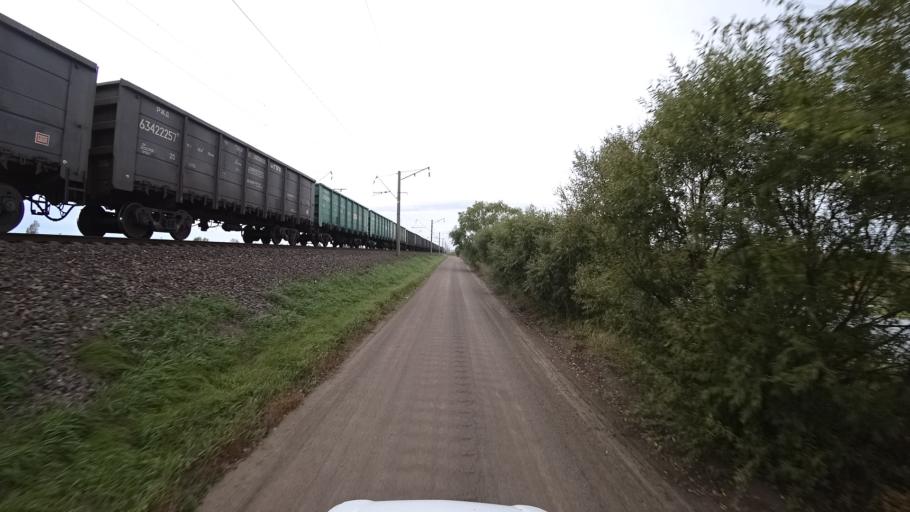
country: RU
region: Amur
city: Arkhara
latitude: 49.3622
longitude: 130.1484
